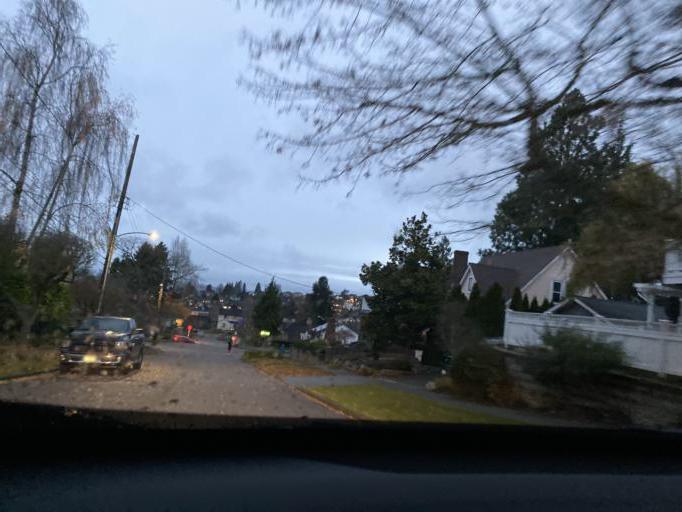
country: US
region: Washington
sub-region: King County
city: Seattle
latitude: 47.6367
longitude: -122.3933
